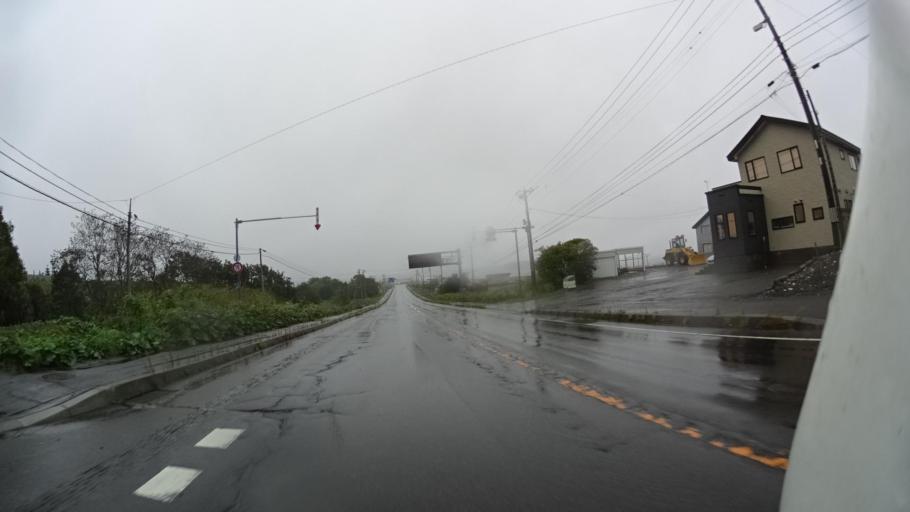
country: JP
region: Hokkaido
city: Nemuro
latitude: 43.2776
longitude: 145.5045
